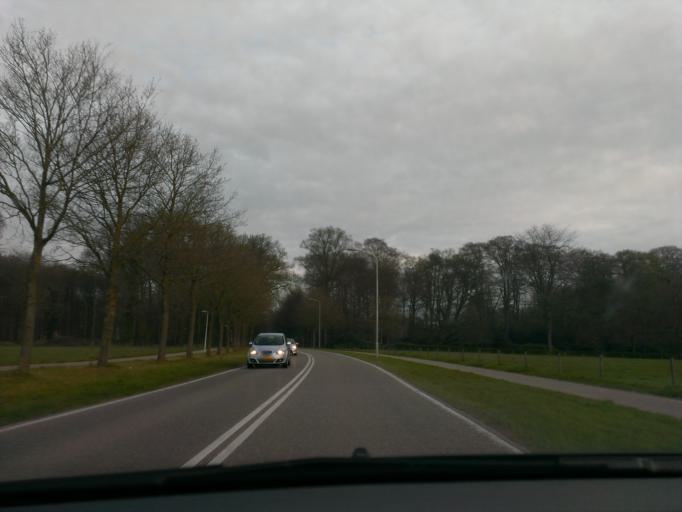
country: NL
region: Gelderland
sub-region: Gemeente Voorst
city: Twello
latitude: 52.2185
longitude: 6.1148
